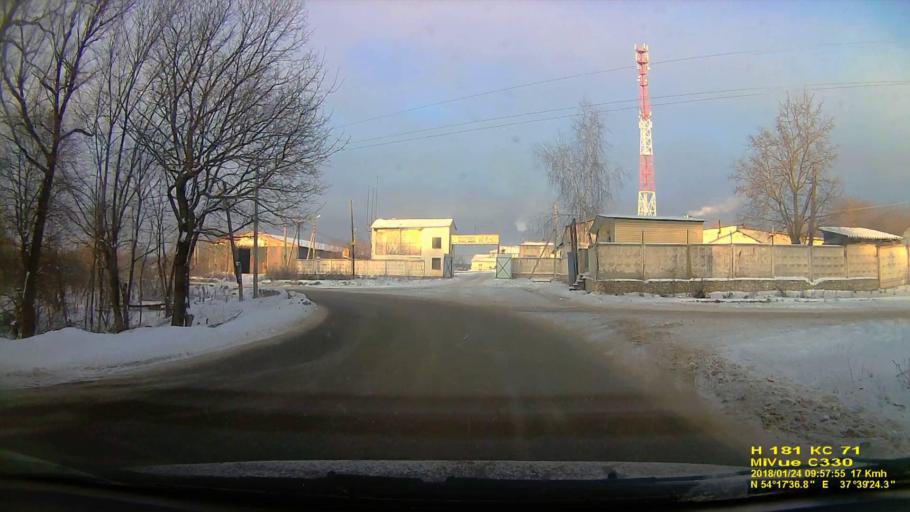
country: RU
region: Tula
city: Gorelki
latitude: 54.2935
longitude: 37.6566
